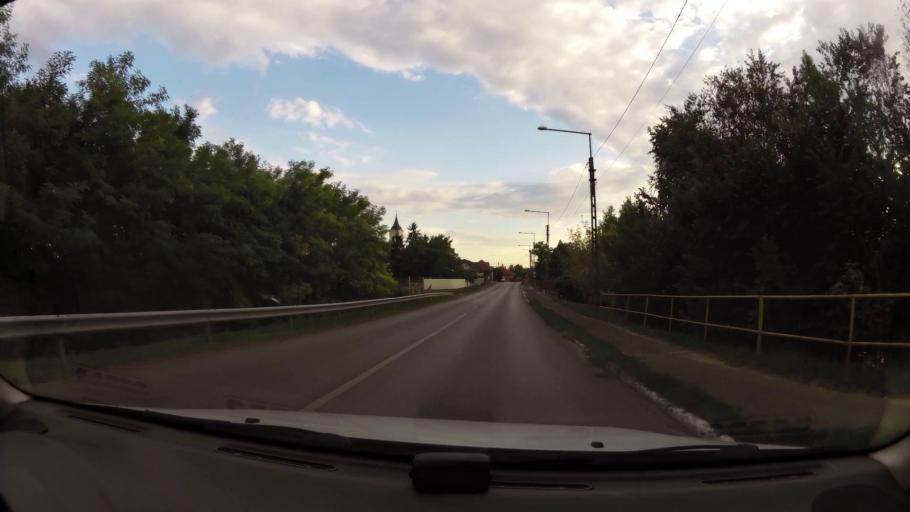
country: HU
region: Pest
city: Tapiobicske
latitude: 47.3636
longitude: 19.6882
